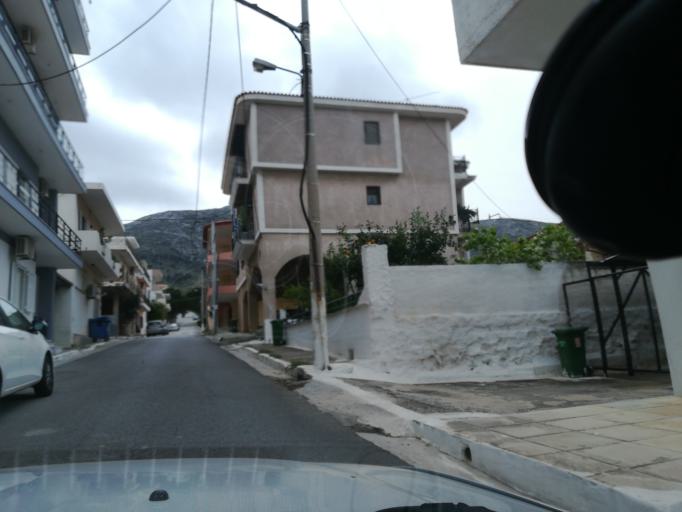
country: GR
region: Attica
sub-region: Nomarchia Anatolikis Attikis
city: Keratea
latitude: 37.8035
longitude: 23.9796
